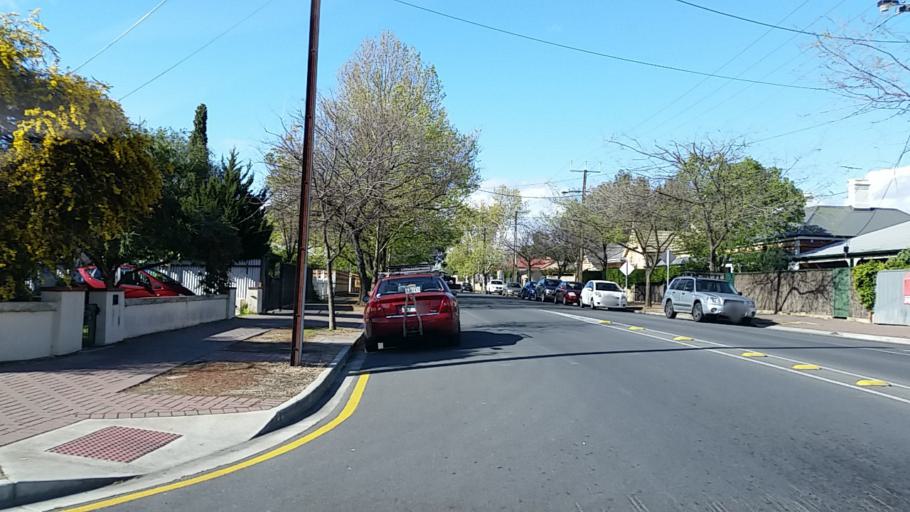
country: AU
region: South Australia
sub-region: Norwood Payneham St Peters
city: Royston Park
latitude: -34.9086
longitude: 138.6163
